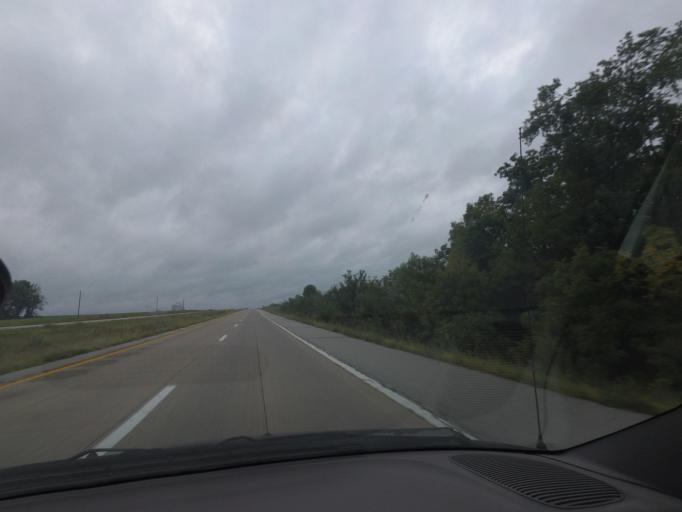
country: US
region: Missouri
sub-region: Marion County
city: Monroe City
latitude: 39.6735
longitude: -91.8744
